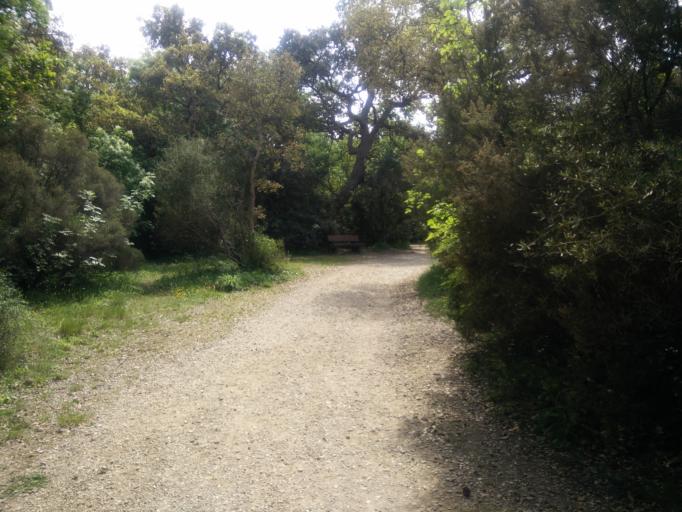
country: FR
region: Provence-Alpes-Cote d'Azur
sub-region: Departement des Alpes-Maritimes
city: Biot
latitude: 43.6234
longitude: 7.1224
